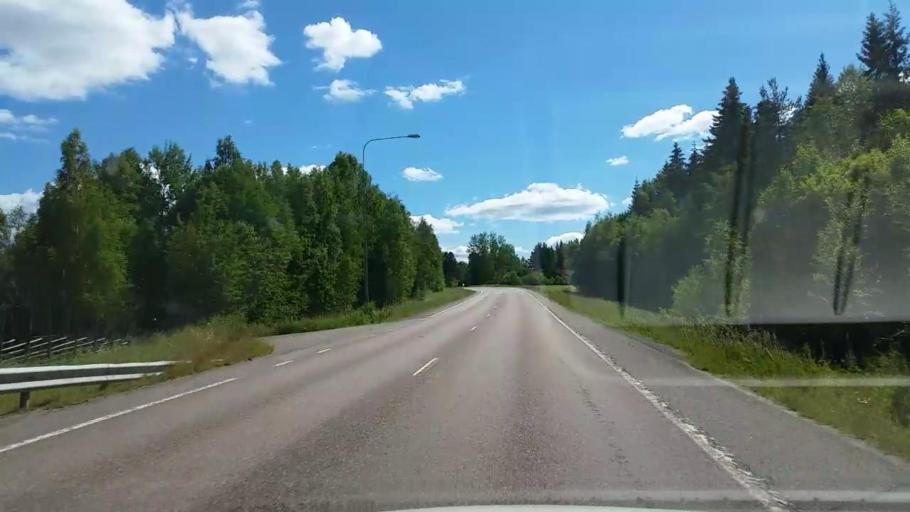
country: SE
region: Dalarna
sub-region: Faluns Kommun
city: Svardsjo
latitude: 60.8308
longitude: 15.7604
